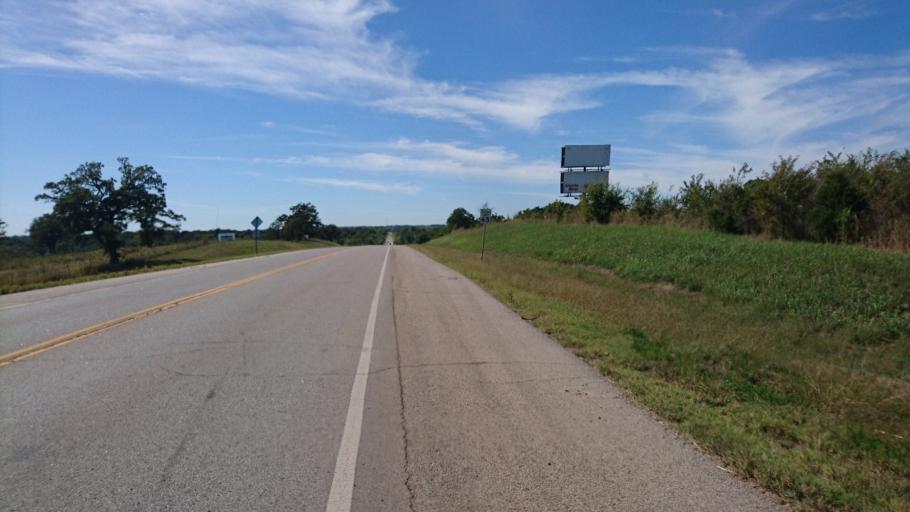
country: US
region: Oklahoma
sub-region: Lincoln County
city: Stroud
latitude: 35.7241
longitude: -96.7351
